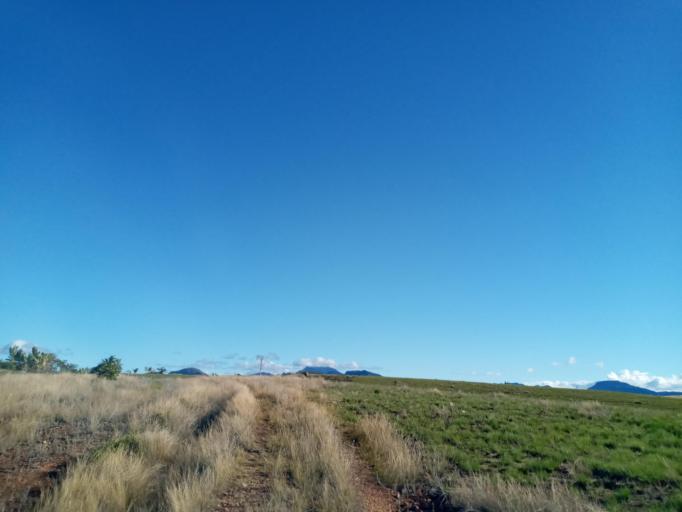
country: MG
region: Anosy
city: Fort Dauphin
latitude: -24.4063
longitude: 47.2550
